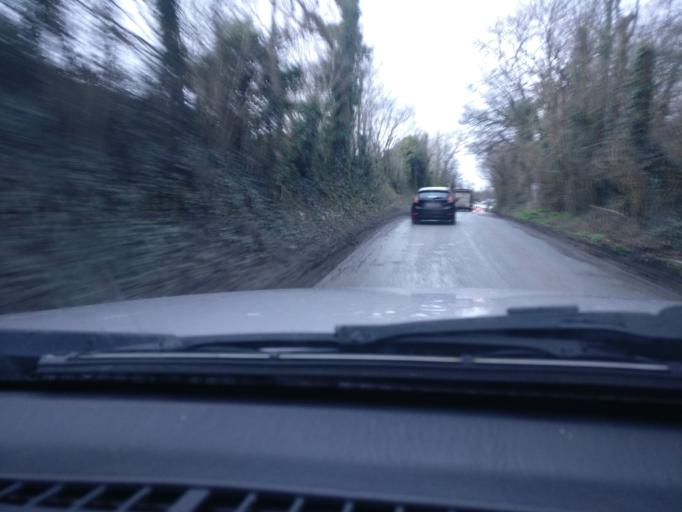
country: IE
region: Leinster
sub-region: An Mhi
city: Longwood
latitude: 53.4375
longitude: -6.9882
